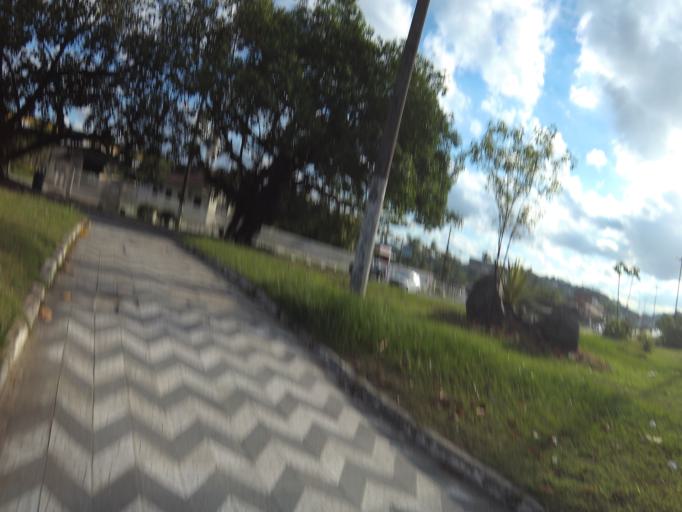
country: BR
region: Santa Catarina
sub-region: Blumenau
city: Blumenau
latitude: -26.8713
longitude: -49.0946
